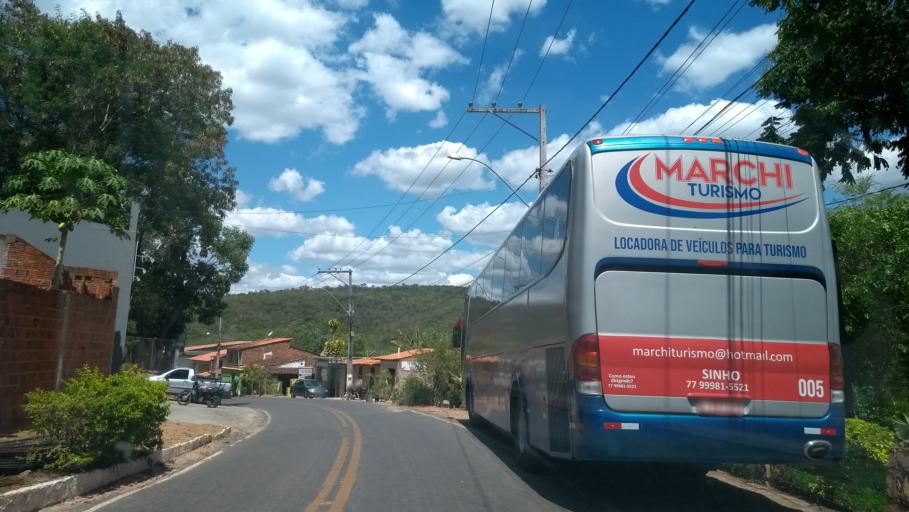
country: BR
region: Bahia
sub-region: Andarai
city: Vera Cruz
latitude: -12.5603
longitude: -41.3854
